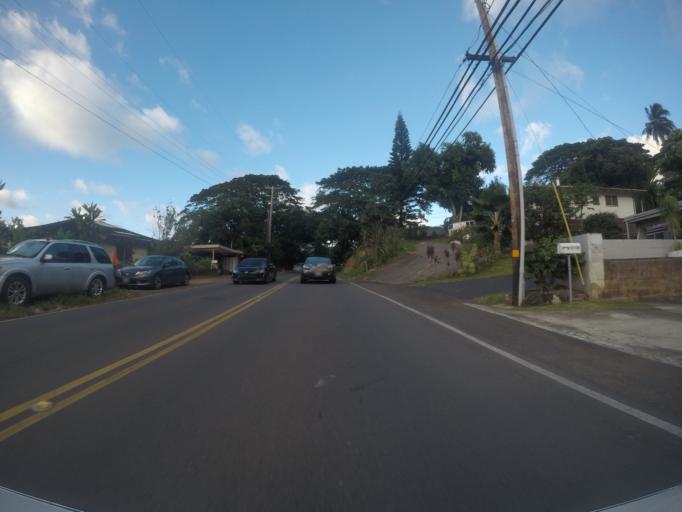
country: US
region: Hawaii
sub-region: Honolulu County
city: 'Ahuimanu
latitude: 21.4520
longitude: -157.8224
